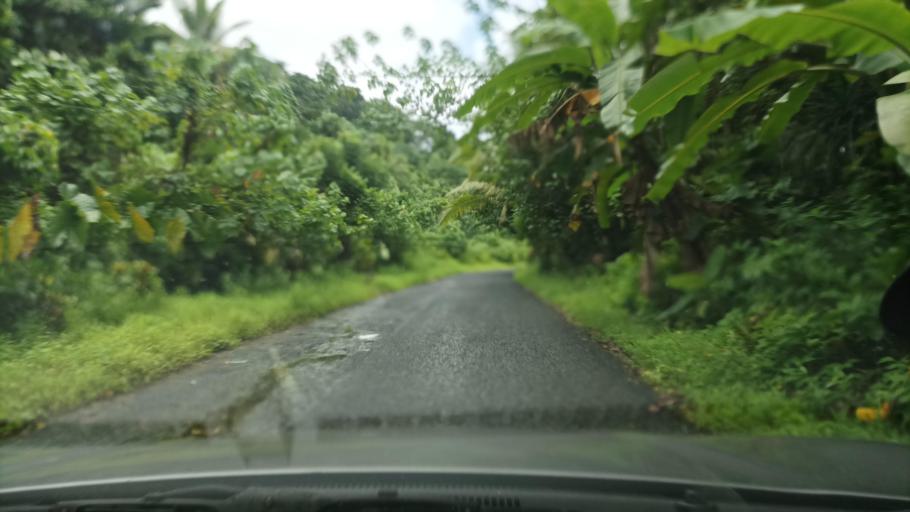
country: FM
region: Pohnpei
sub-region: Madolenihm Municipality
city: Madolenihm Municipality Government
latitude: 6.8469
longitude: 158.3014
